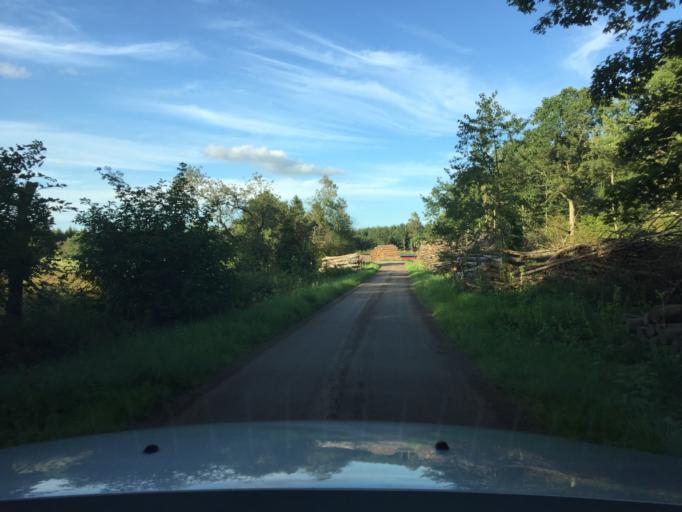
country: SE
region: Skane
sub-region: Hassleholms Kommun
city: Sosdala
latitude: 56.0253
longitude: 13.6918
